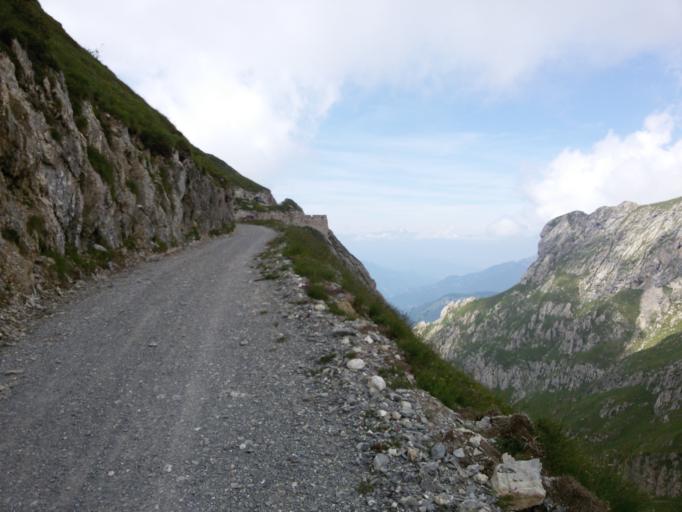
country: IT
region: Piedmont
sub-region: Provincia di Cuneo
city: Limone Piemonte
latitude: 44.1648
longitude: 7.6263
